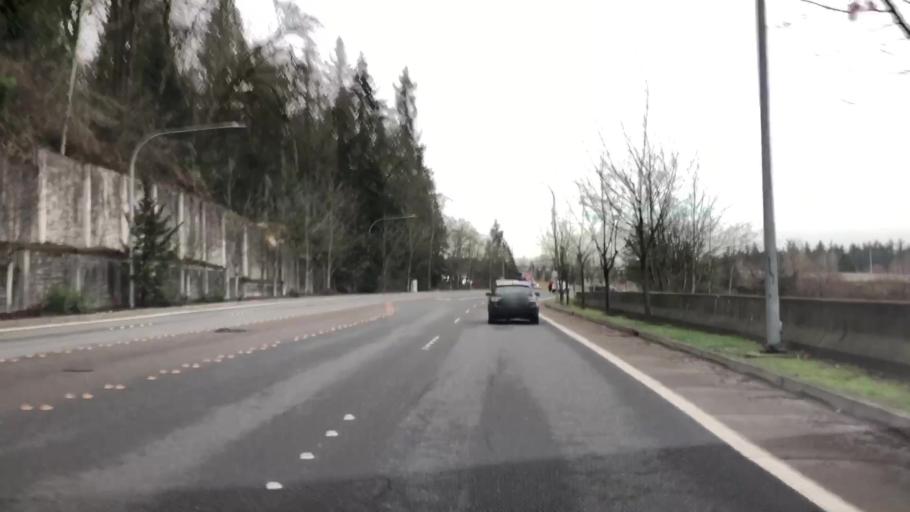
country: US
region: Washington
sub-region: King County
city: Redmond
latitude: 47.6636
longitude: -122.1269
